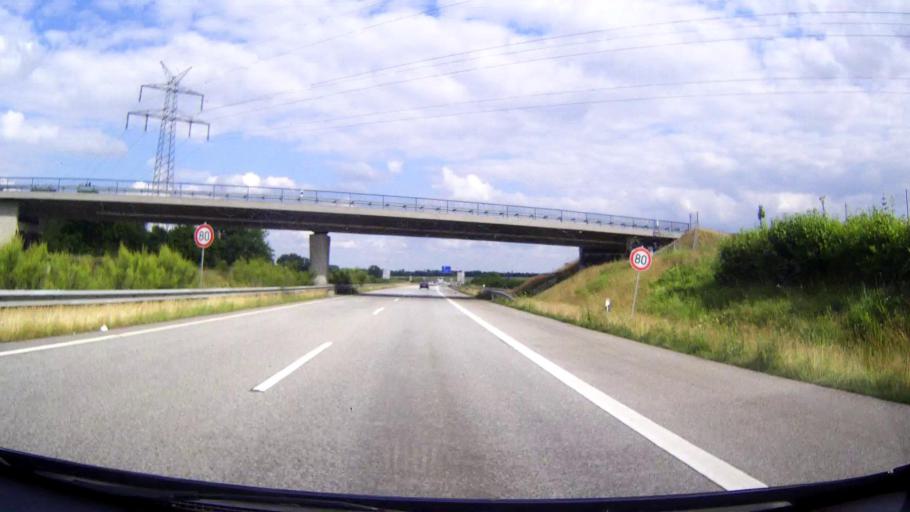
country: DE
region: Schleswig-Holstein
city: Monkhagen
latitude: 53.9110
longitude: 10.5525
